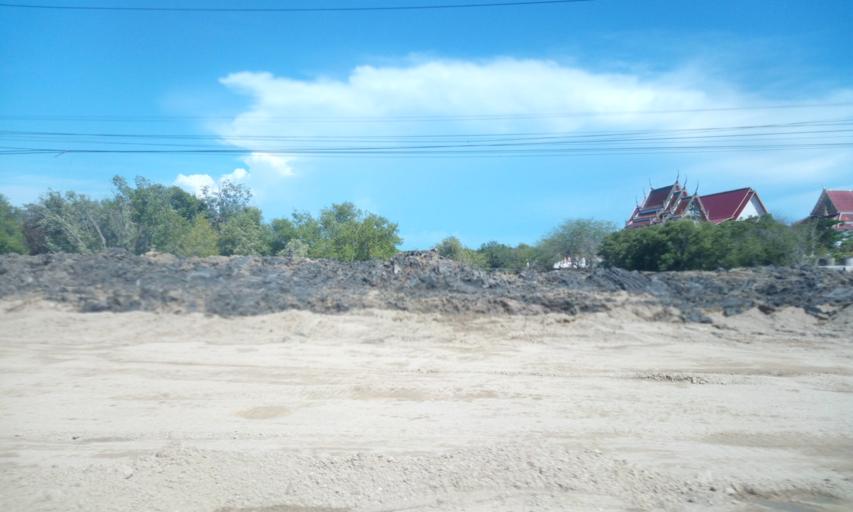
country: TH
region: Samut Prakan
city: Bang Bo District
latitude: 13.5044
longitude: 100.7776
